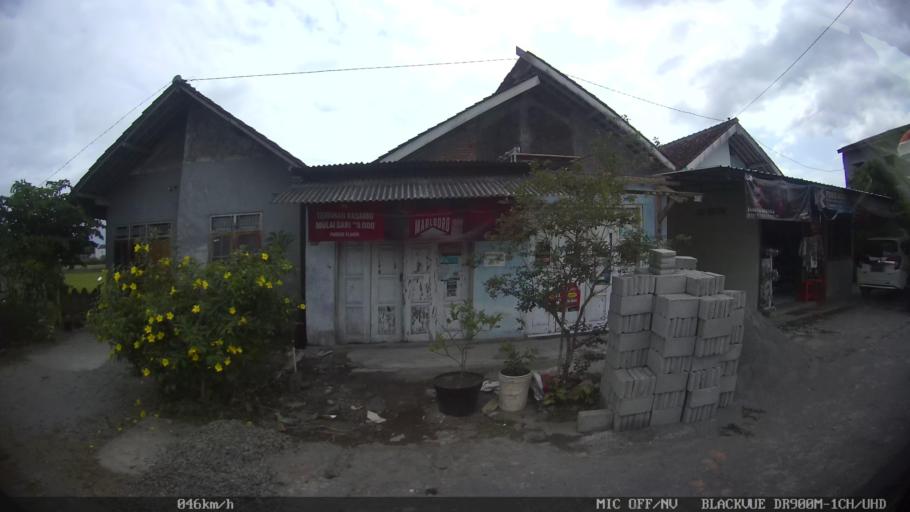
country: ID
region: Daerah Istimewa Yogyakarta
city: Depok
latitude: -7.8107
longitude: 110.4633
